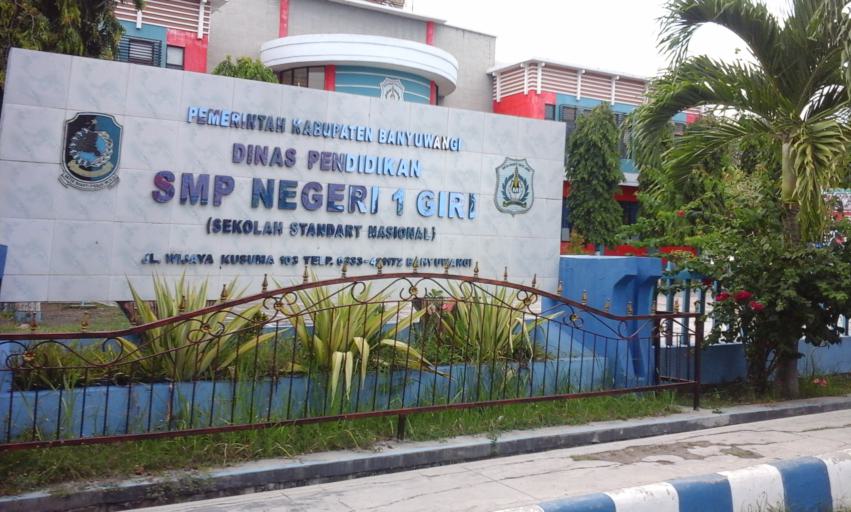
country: ID
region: East Java
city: Krajan Satu
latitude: -8.2092
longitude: 114.3510
